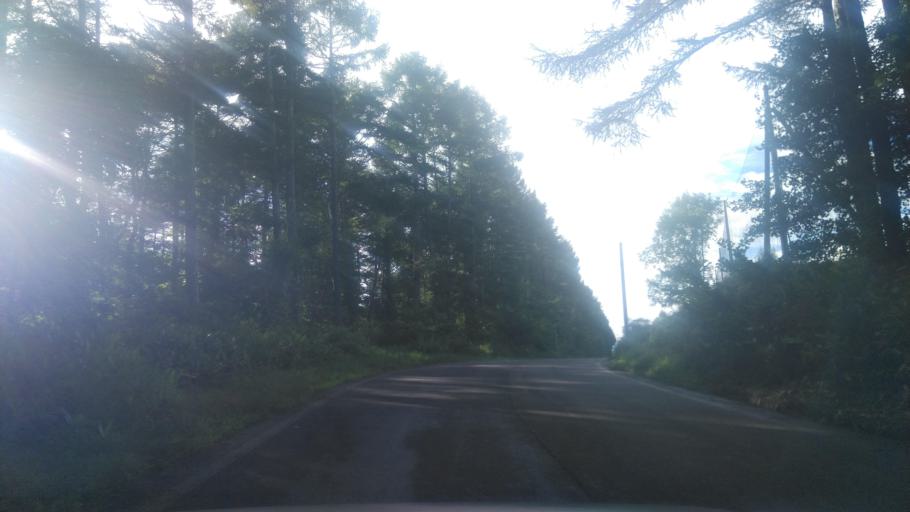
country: JP
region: Nagano
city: Suzaka
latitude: 36.5217
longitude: 138.3535
